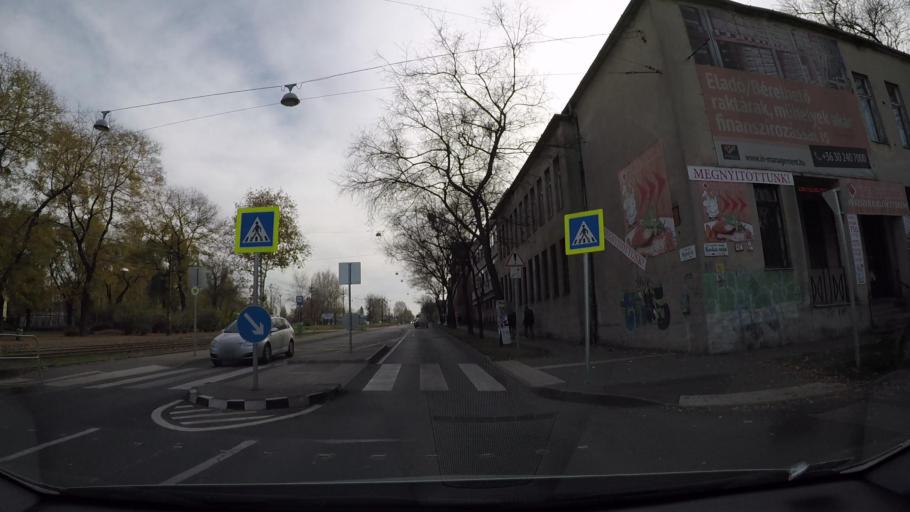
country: HU
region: Budapest
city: Budapest X. keruelet
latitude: 47.4849
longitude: 19.1556
